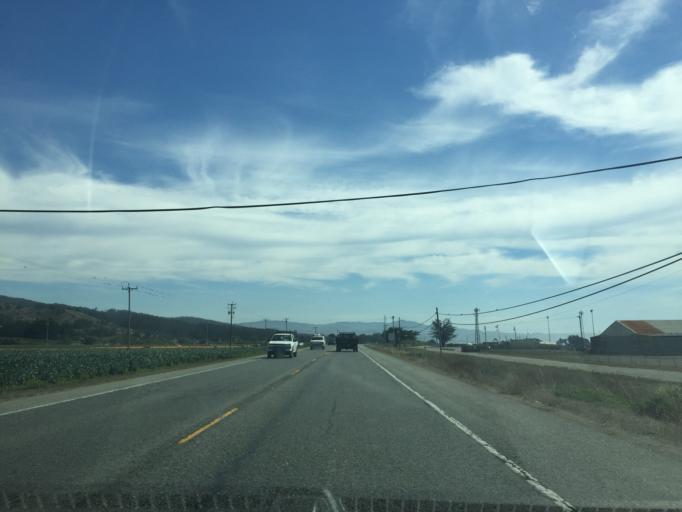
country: US
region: California
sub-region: San Mateo County
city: Moss Beach
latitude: 37.5159
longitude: -122.4970
